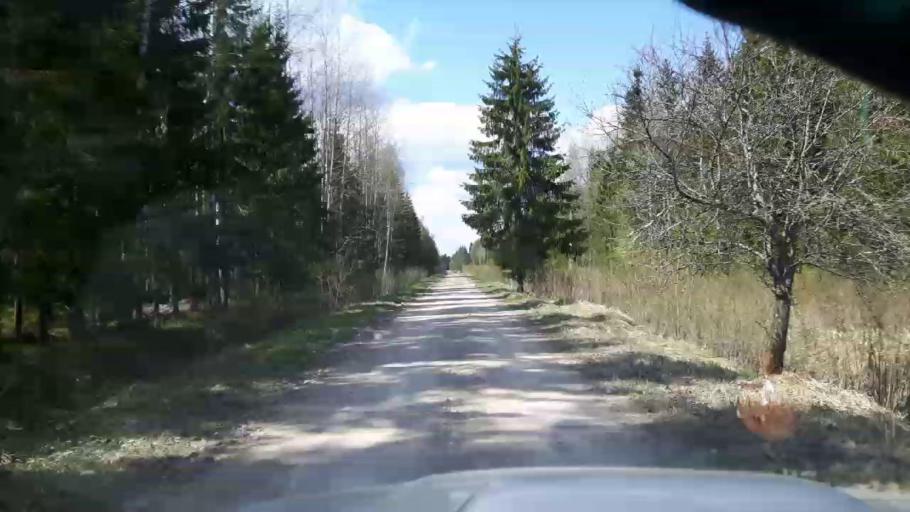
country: EE
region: Paernumaa
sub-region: Tootsi vald
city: Tootsi
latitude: 58.4442
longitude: 24.9167
